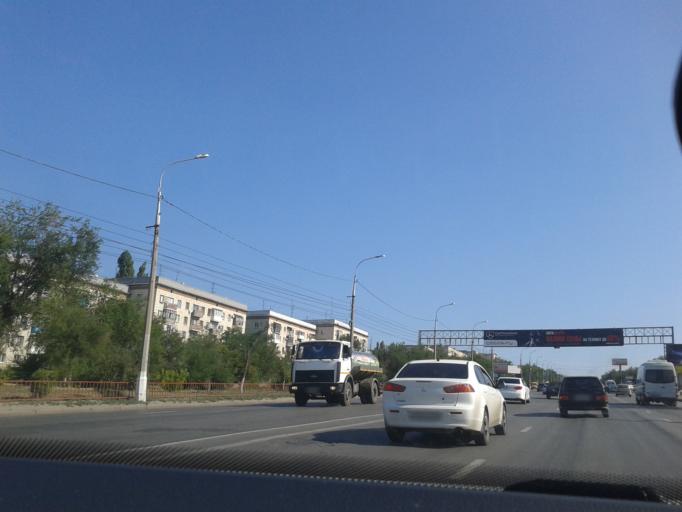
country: RU
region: Volgograd
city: Volgograd
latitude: 48.6630
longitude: 44.4396
